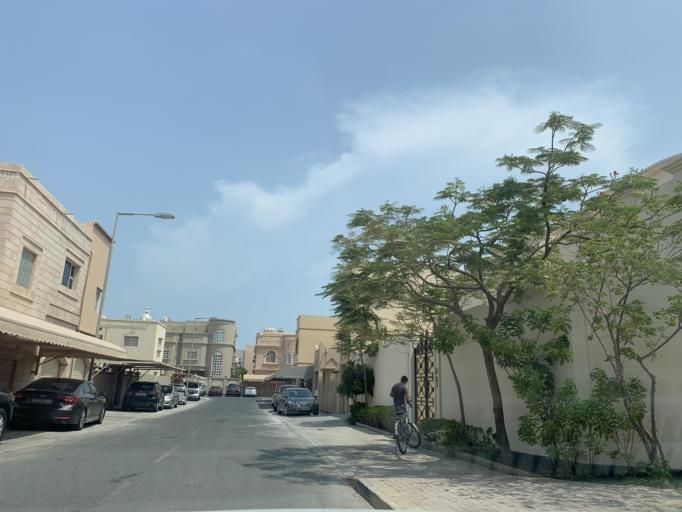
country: BH
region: Muharraq
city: Al Hadd
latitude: 26.2746
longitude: 50.6559
